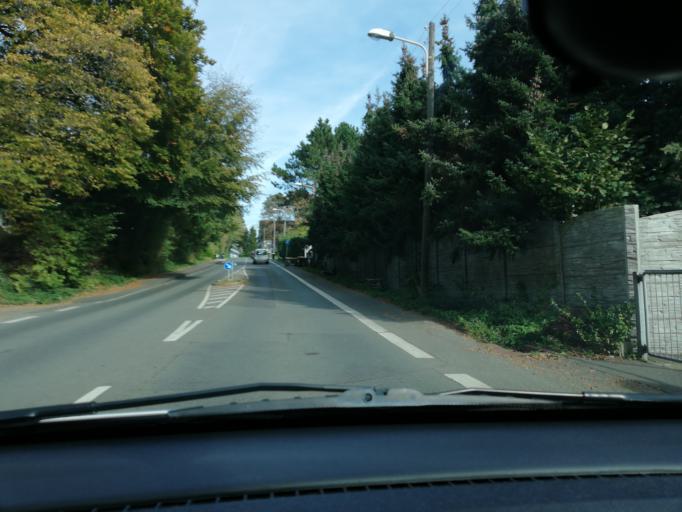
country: DE
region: North Rhine-Westphalia
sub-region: Regierungsbezirk Dusseldorf
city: Wuppertal
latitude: 51.3010
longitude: 7.2099
